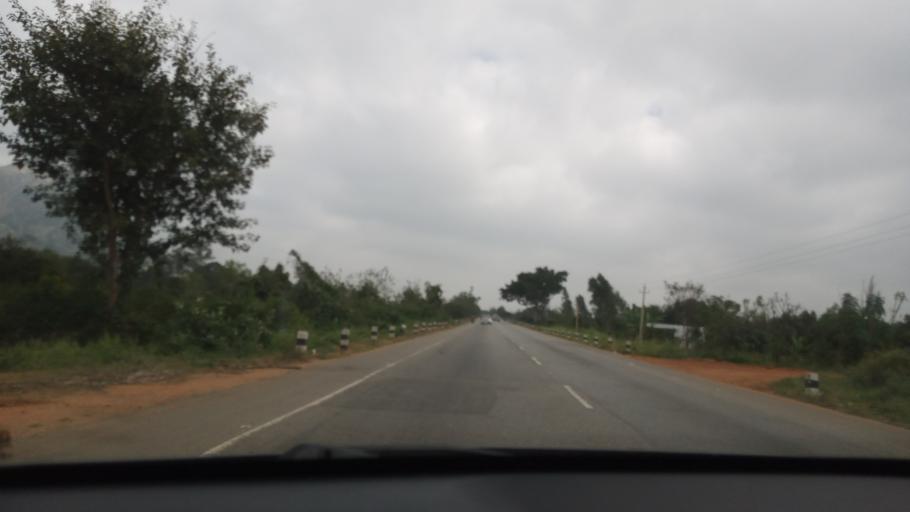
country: IN
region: Karnataka
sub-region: Chikkaballapur
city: Chintamani
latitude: 13.3329
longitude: 78.0005
